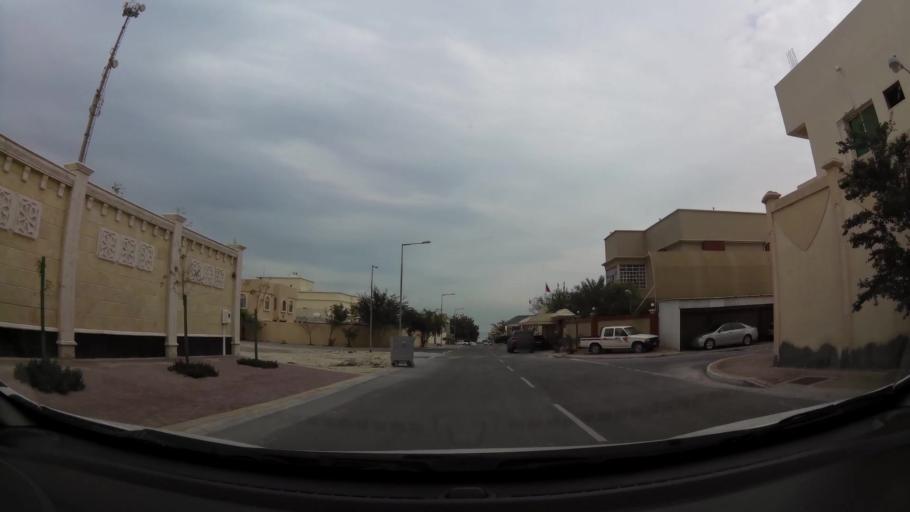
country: BH
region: Northern
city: Ar Rifa'
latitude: 26.0593
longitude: 50.6138
